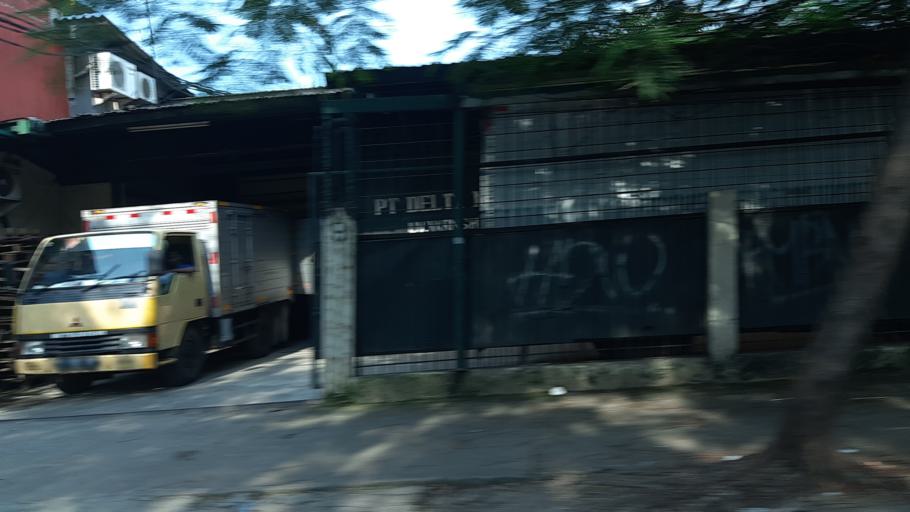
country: ID
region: Jakarta Raya
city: Jakarta
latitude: -6.1706
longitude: 106.7653
